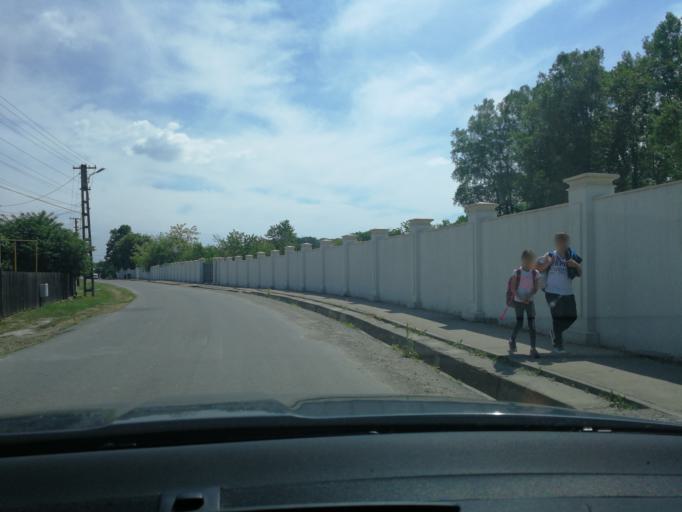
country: RO
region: Prahova
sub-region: Comuna Targsoru Vechi
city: Targsoru Vechi
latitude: 44.8544
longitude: 25.9093
